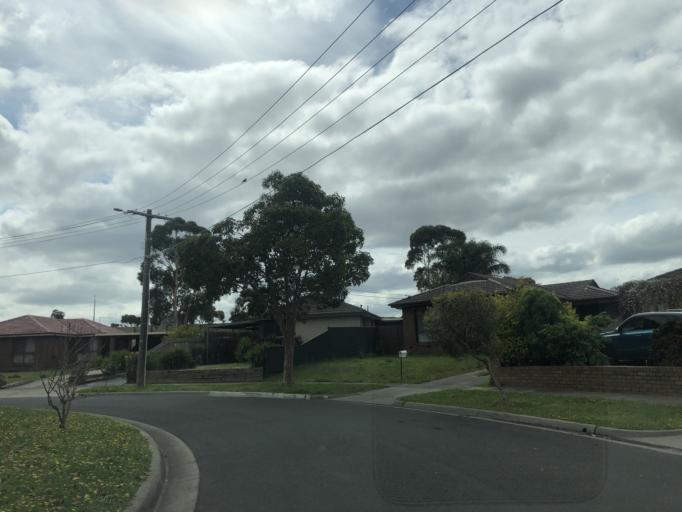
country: AU
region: Victoria
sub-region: Greater Dandenong
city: Dandenong North
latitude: -37.9521
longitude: 145.2105
